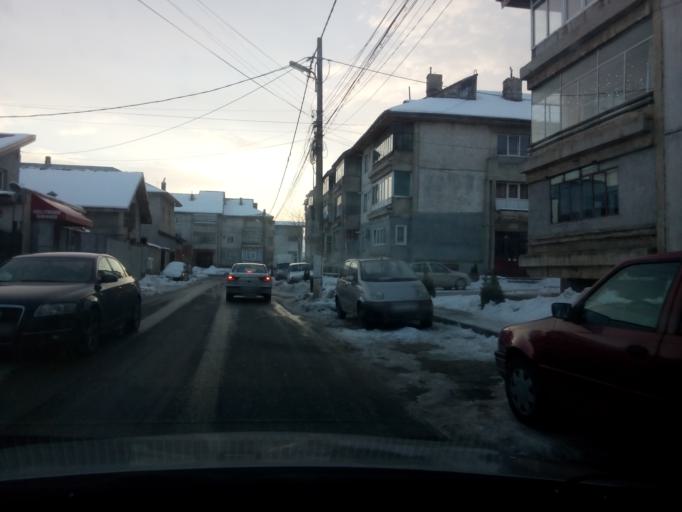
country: RO
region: Ilfov
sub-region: Comuna Pantelimon
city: Pantelimon
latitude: 44.4530
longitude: 26.2069
